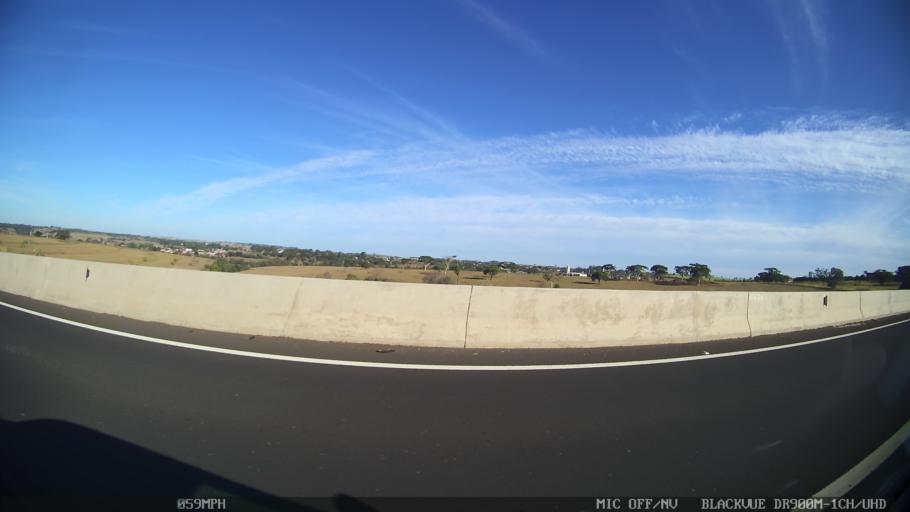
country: BR
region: Sao Paulo
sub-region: Sao Jose Do Rio Preto
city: Sao Jose do Rio Preto
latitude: -20.8503
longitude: -49.3894
